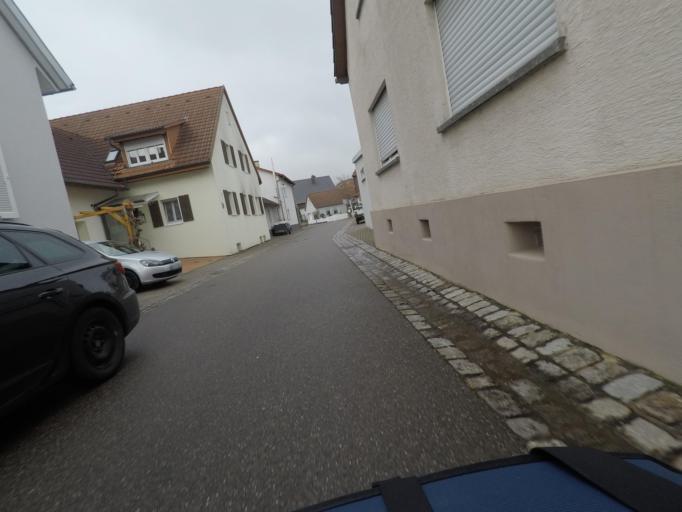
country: DE
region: Baden-Wuerttemberg
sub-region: Karlsruhe Region
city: Au am Rhein
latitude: 48.9528
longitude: 8.2399
